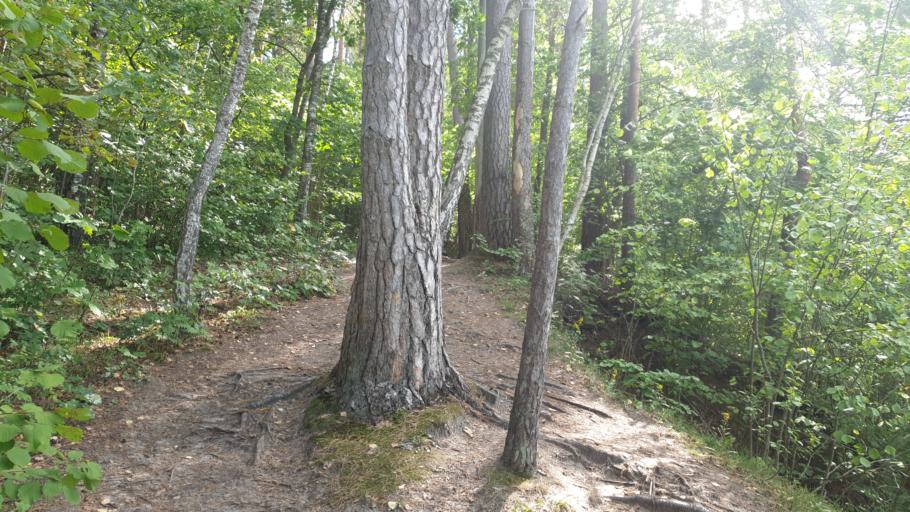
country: LT
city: Grigiskes
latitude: 54.8011
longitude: 24.9785
